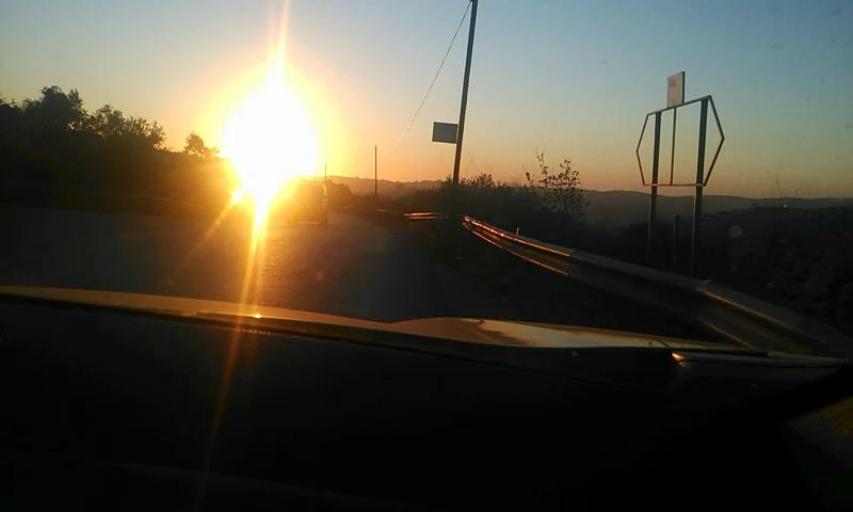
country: PS
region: West Bank
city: `Ayn Yabrud
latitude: 31.9586
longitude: 35.2559
